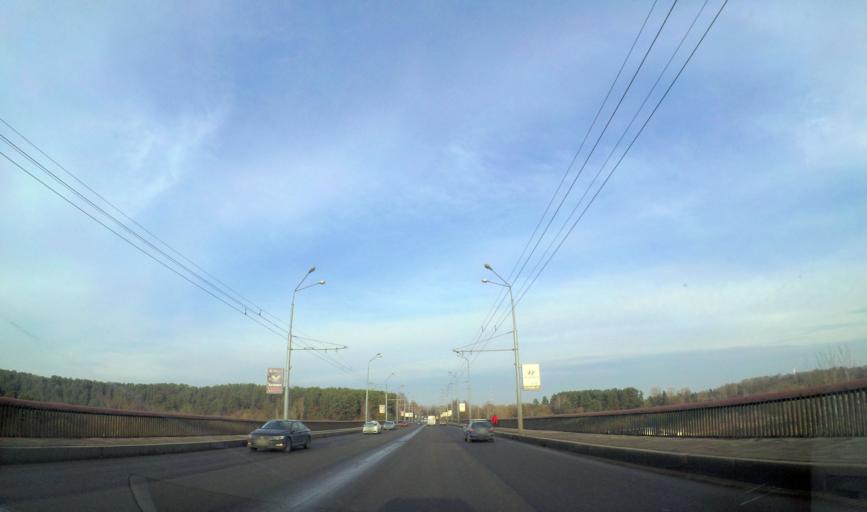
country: BY
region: Grodnenskaya
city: Hrodna
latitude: 53.6779
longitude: 23.8059
